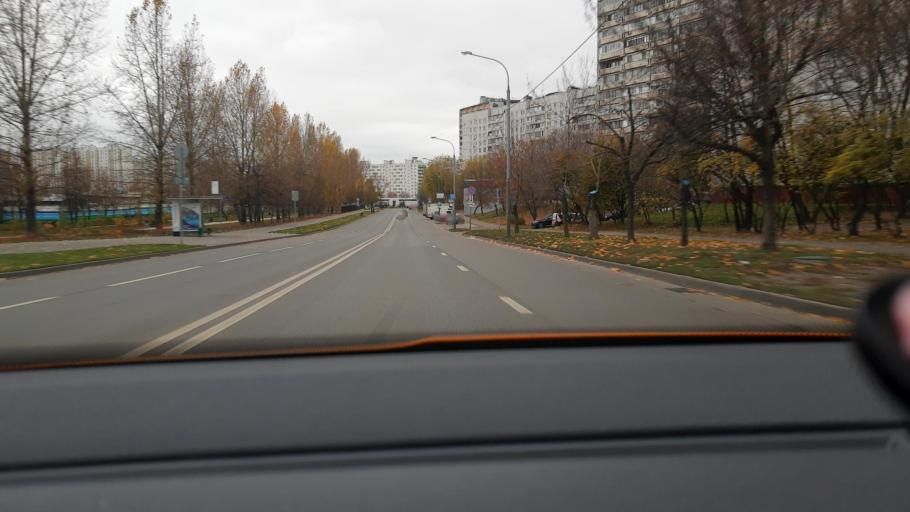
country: RU
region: Moscow
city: Lyublino
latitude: 55.6784
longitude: 37.7764
